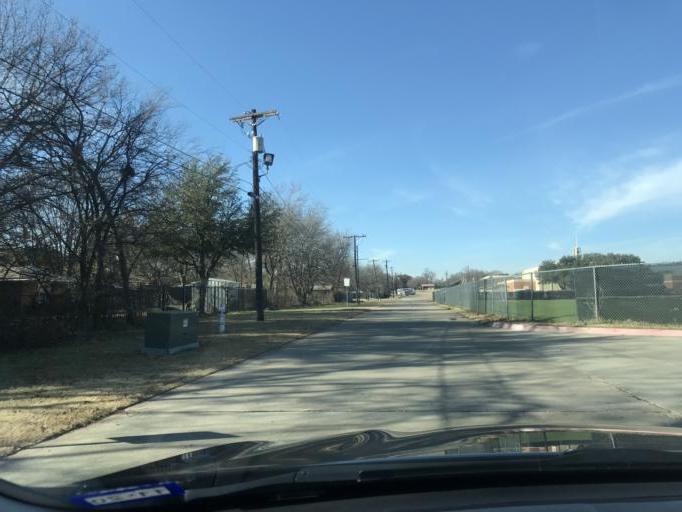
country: US
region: Texas
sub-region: Denton County
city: Denton
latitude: 33.2241
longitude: -97.1460
